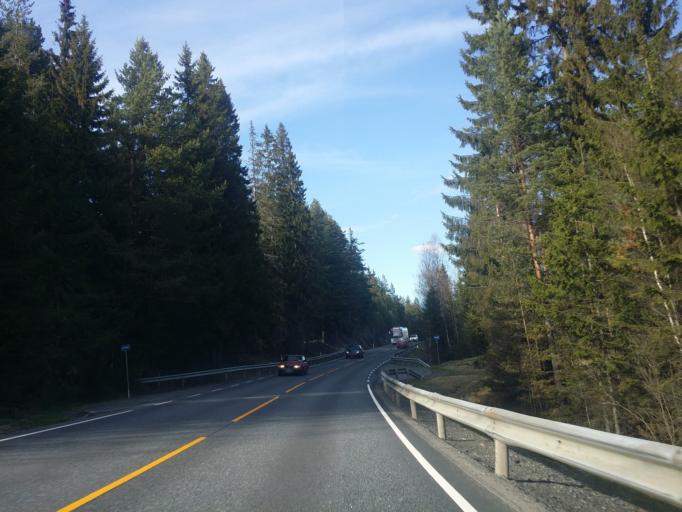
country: NO
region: Buskerud
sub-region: Kongsberg
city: Kongsberg
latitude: 59.6164
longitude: 9.4669
